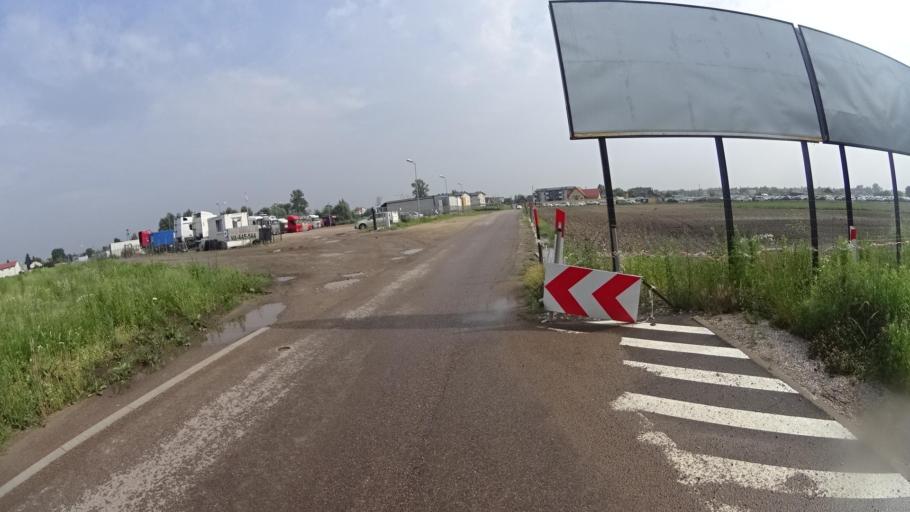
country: PL
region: Masovian Voivodeship
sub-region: Powiat pruszkowski
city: Nowe Grocholice
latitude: 52.1692
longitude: 20.9195
